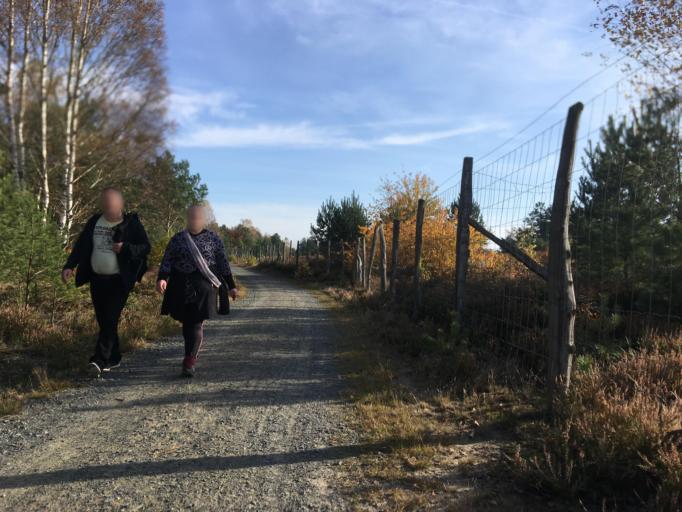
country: DE
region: Berlin
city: Buch
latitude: 52.6943
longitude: 13.5060
